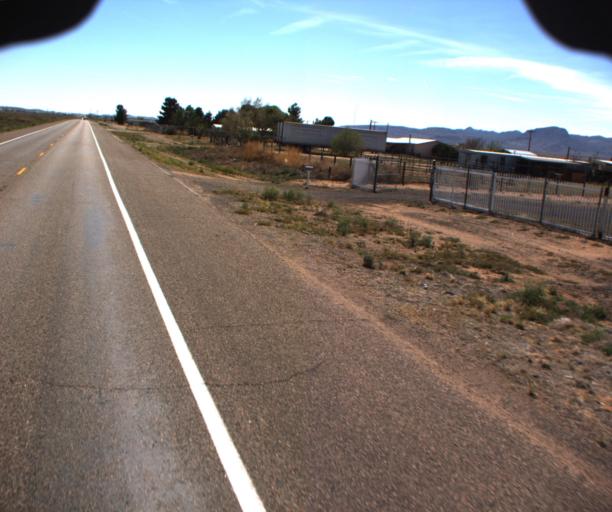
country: US
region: Arizona
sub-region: Mohave County
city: New Kingman-Butler
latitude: 35.2917
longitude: -113.9396
